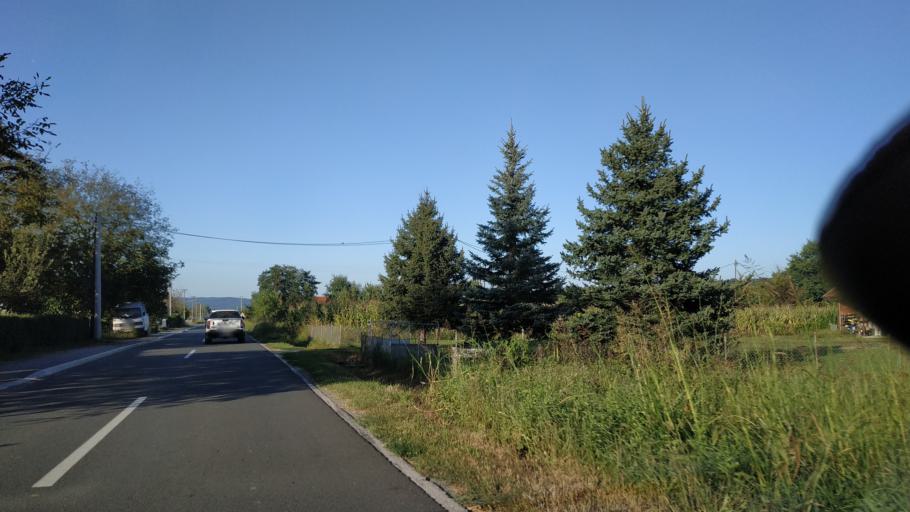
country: RS
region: Central Serbia
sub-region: Rasinski Okrug
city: Krusevac
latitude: 43.5309
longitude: 21.3414
